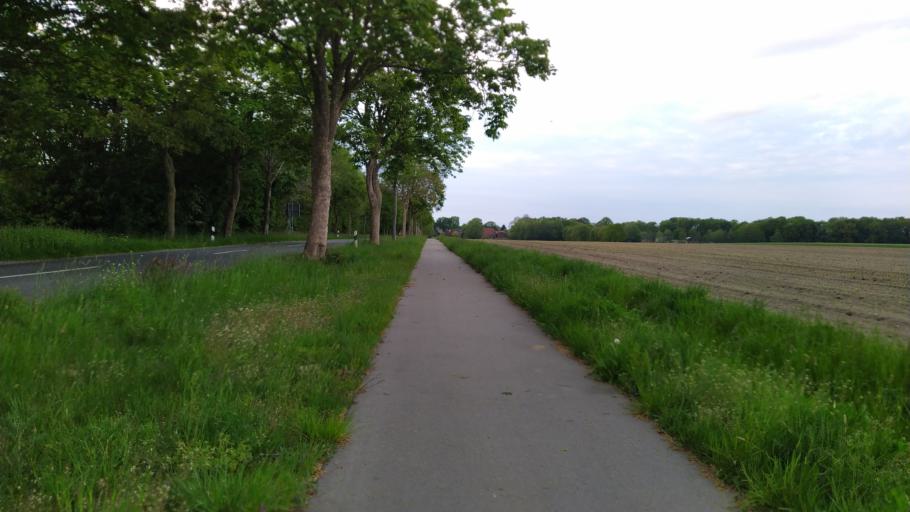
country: DE
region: Lower Saxony
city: Ahlerstedt
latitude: 53.3970
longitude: 9.4043
